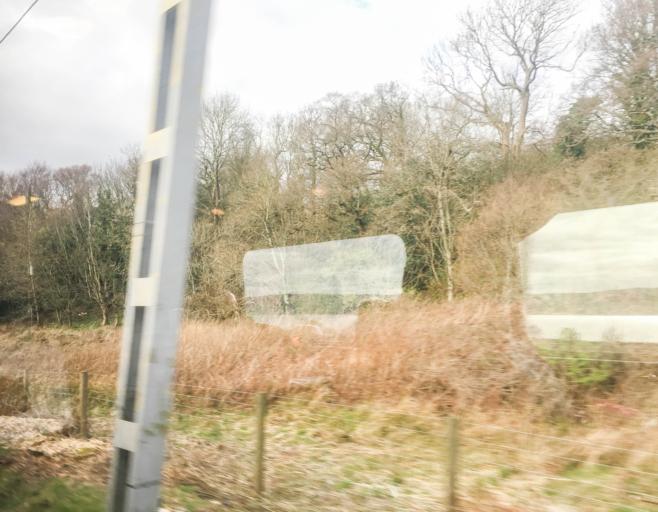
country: GB
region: Scotland
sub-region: Argyll and Bute
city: Cardross
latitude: 55.9482
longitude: -4.6106
